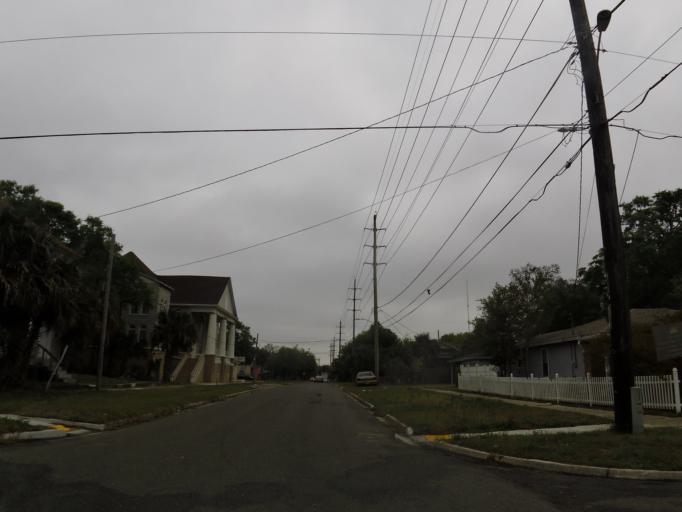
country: US
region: Florida
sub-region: Duval County
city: Jacksonville
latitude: 30.3330
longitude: -81.6394
